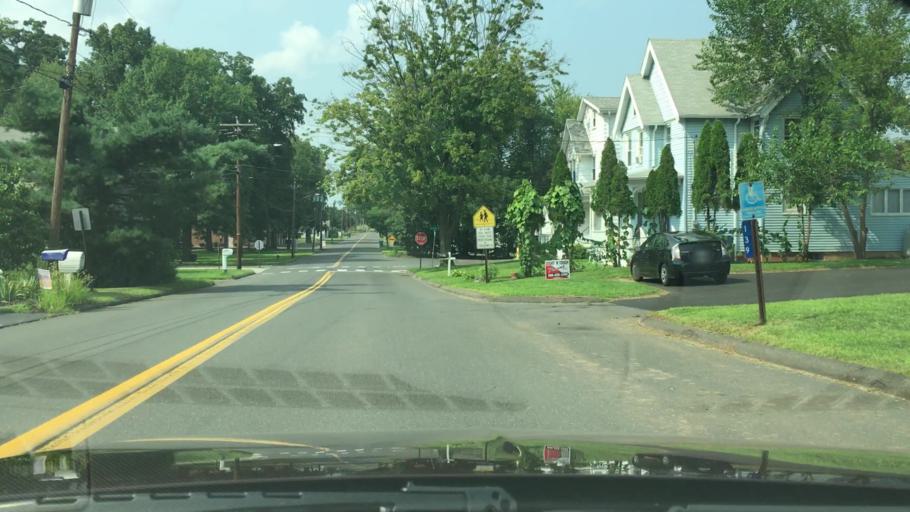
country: US
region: Connecticut
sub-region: Hartford County
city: Kensington
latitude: 41.6142
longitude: -72.7176
